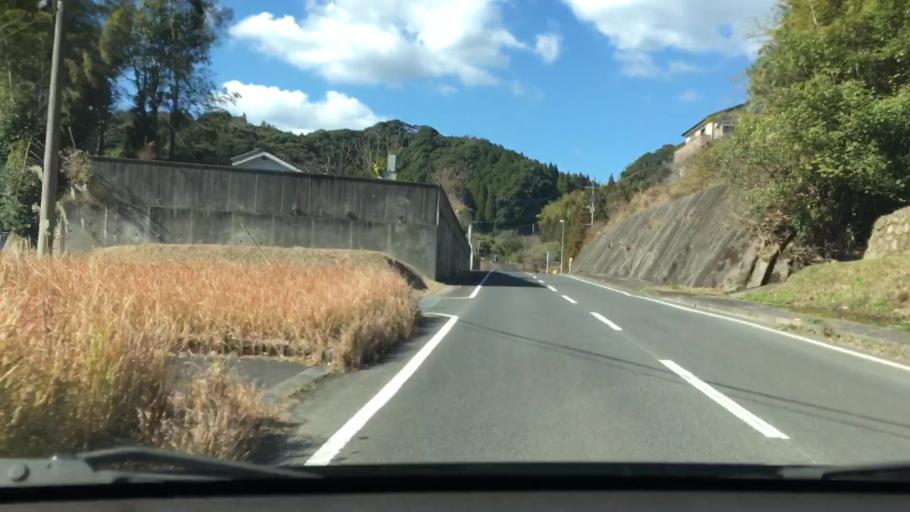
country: JP
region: Kagoshima
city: Ijuin
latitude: 31.6993
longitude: 130.4586
